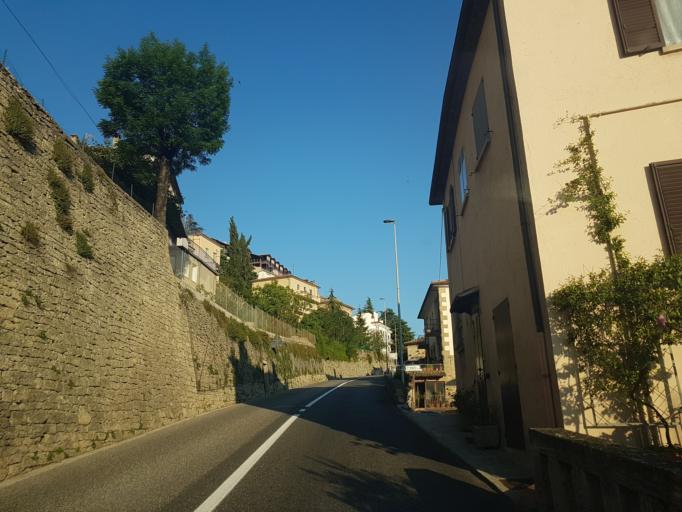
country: SM
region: San Marino
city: San Marino
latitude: 43.9370
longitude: 12.4435
